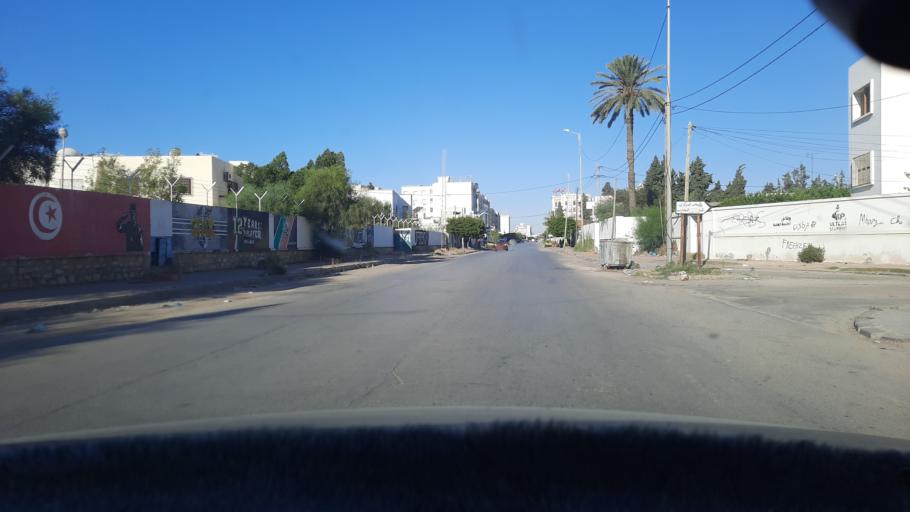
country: TN
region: Safaqis
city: Sfax
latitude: 34.7315
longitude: 10.7442
